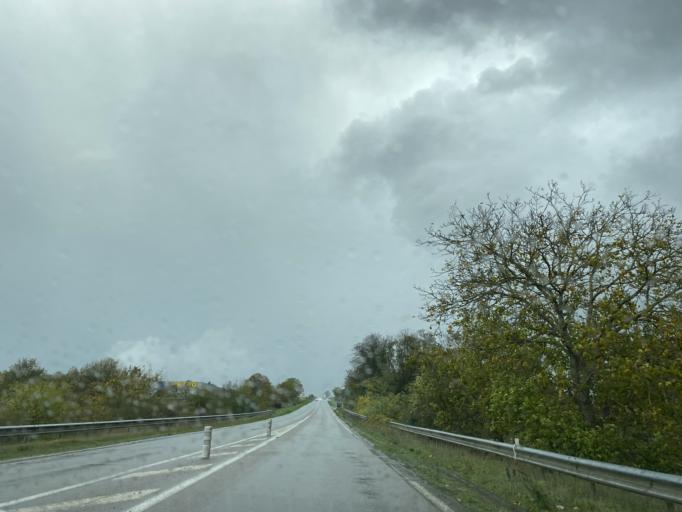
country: FR
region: Centre
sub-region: Departement du Cher
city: La Chapelle-Saint-Ursin
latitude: 47.0546
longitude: 2.3535
